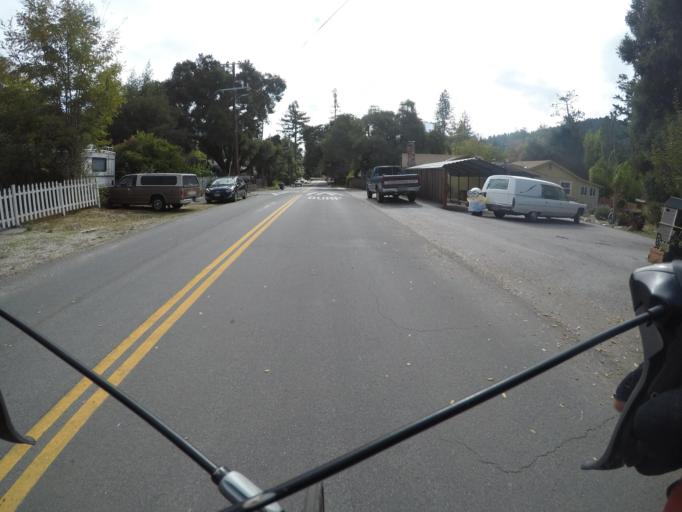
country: US
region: California
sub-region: Santa Cruz County
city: Ben Lomond
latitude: 37.0904
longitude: -122.0855
